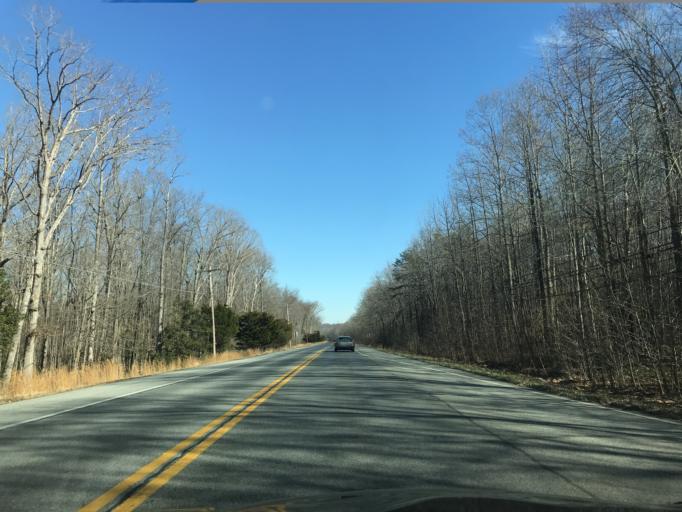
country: US
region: Maryland
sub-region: Charles County
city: Potomac Heights
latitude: 38.5813
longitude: -77.1291
